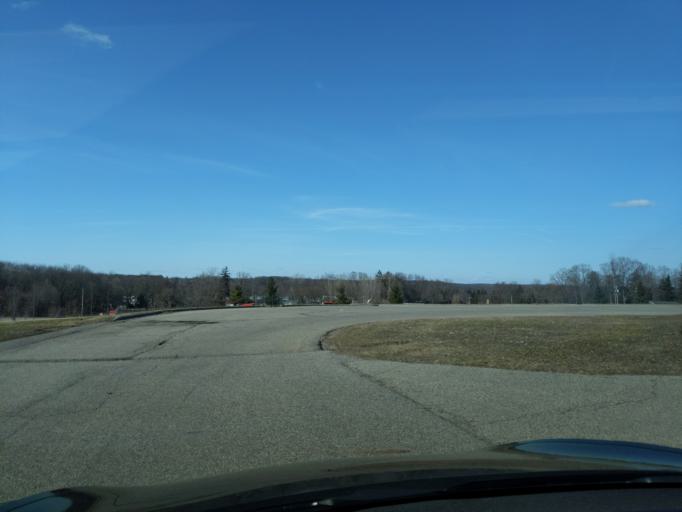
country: US
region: Michigan
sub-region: Ionia County
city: Saranac
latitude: 42.9259
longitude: -85.2017
